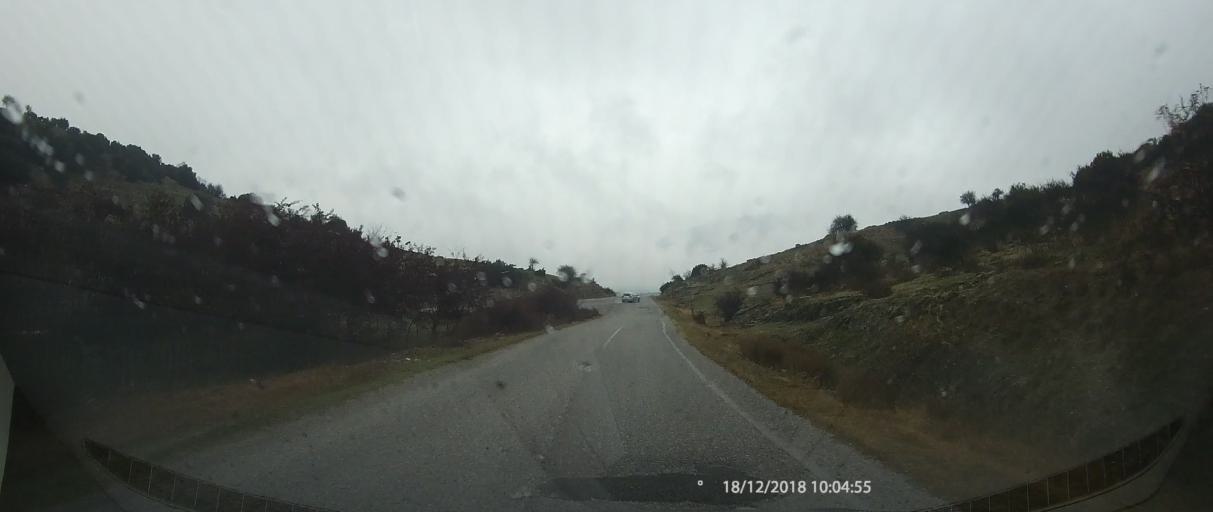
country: GR
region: Thessaly
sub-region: Nomos Larisis
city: Livadi
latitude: 40.0568
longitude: 22.2214
